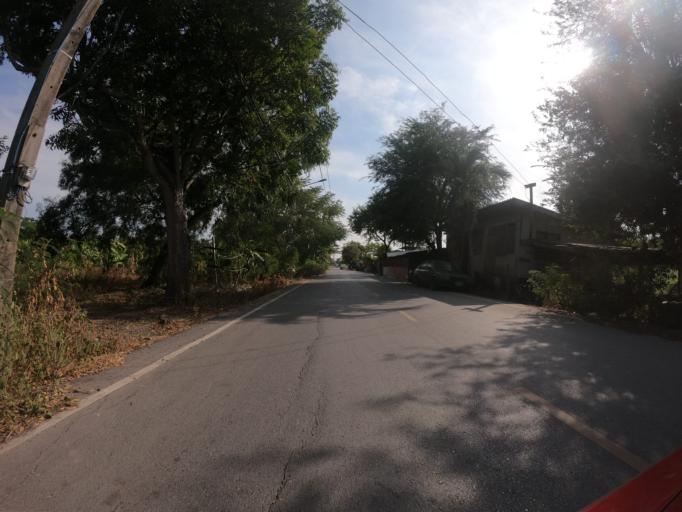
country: TH
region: Pathum Thani
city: Thanyaburi
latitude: 14.0054
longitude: 100.7312
